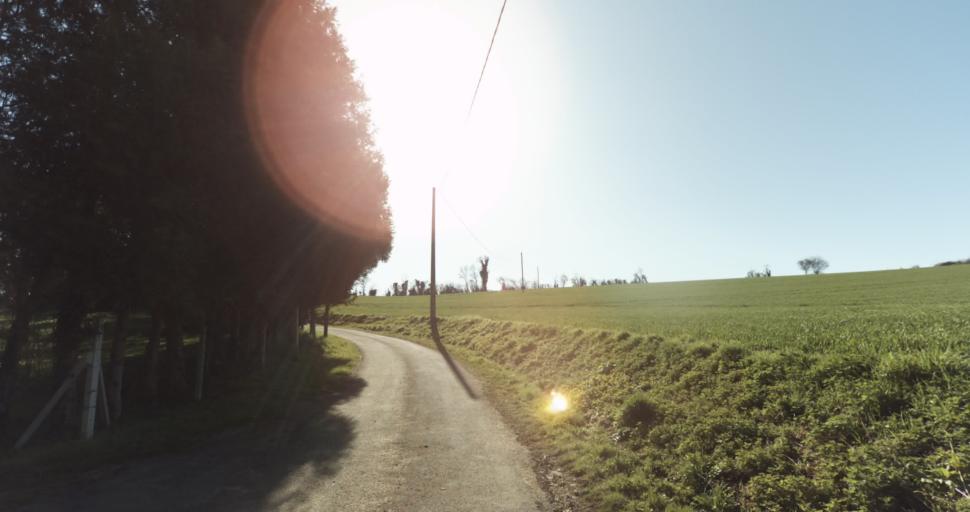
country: FR
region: Lower Normandy
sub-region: Departement du Calvados
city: Saint-Pierre-sur-Dives
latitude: 48.9498
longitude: 0.0244
